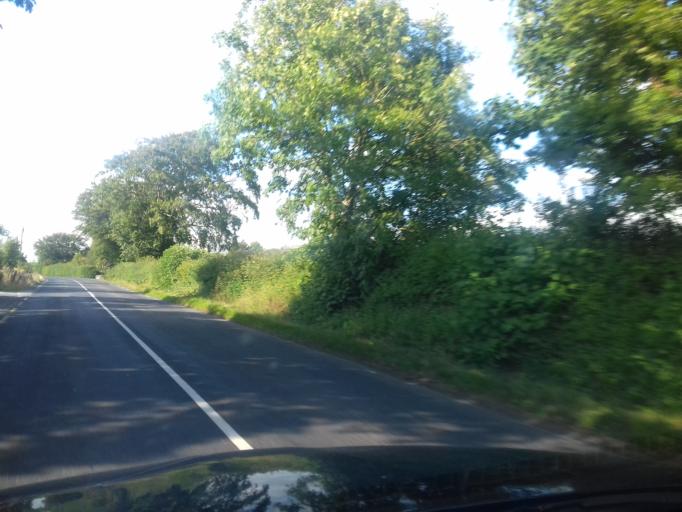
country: IE
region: Leinster
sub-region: Loch Garman
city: New Ross
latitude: 52.4464
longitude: -6.9627
